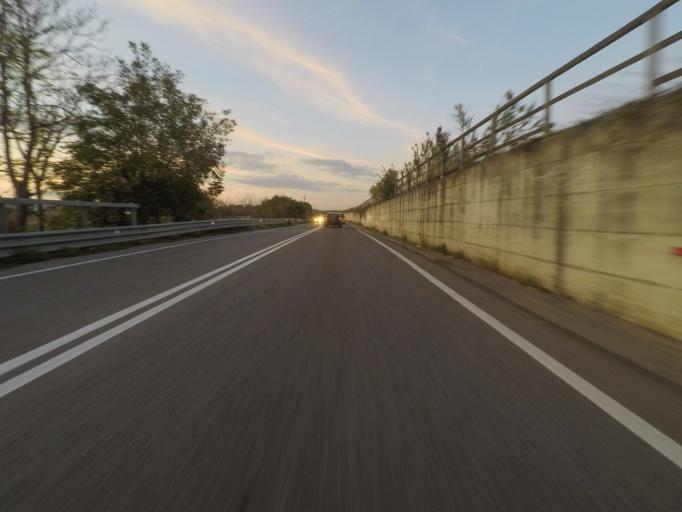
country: IT
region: Tuscany
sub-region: Provincia di Siena
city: Sinalunga
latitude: 43.2080
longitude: 11.7618
